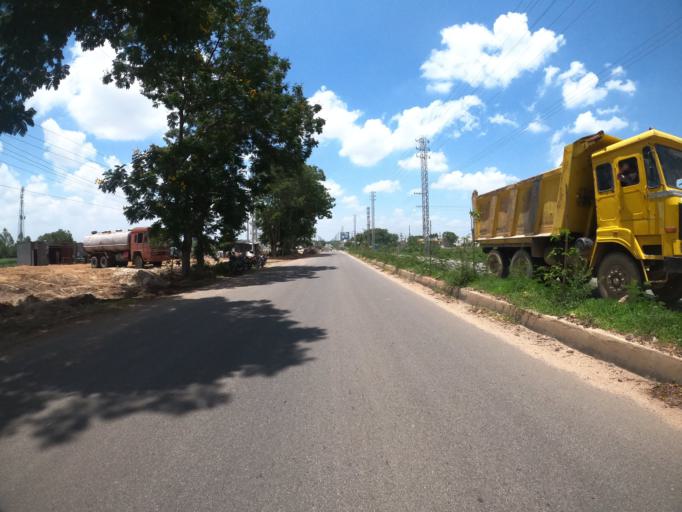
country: IN
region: Telangana
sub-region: Medak
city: Serilingampalle
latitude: 17.4051
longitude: 78.2847
